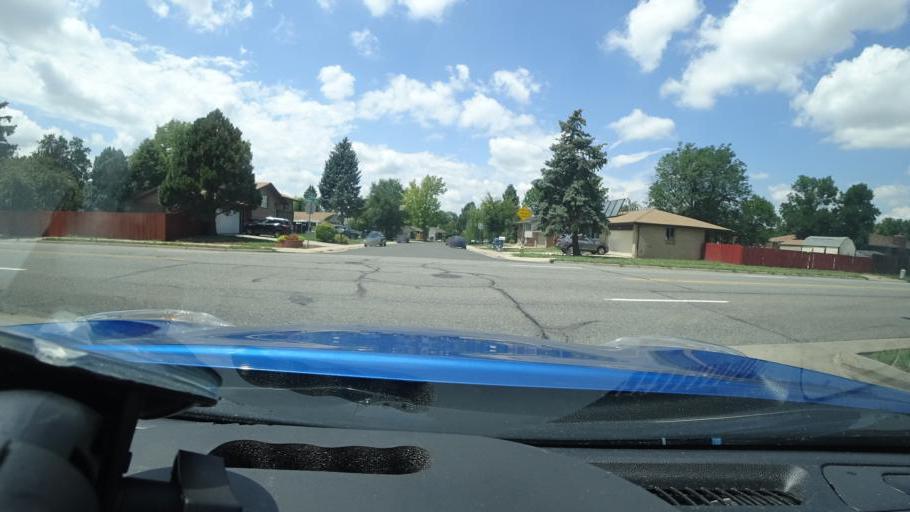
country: US
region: Colorado
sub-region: Adams County
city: Aurora
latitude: 39.7090
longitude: -104.8470
